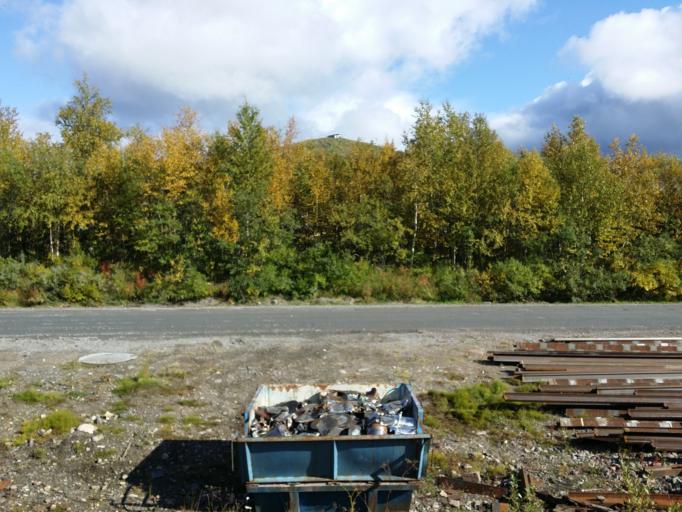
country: SE
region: Norrbotten
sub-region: Kiruna Kommun
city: Kiruna
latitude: 67.8710
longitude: 20.1961
